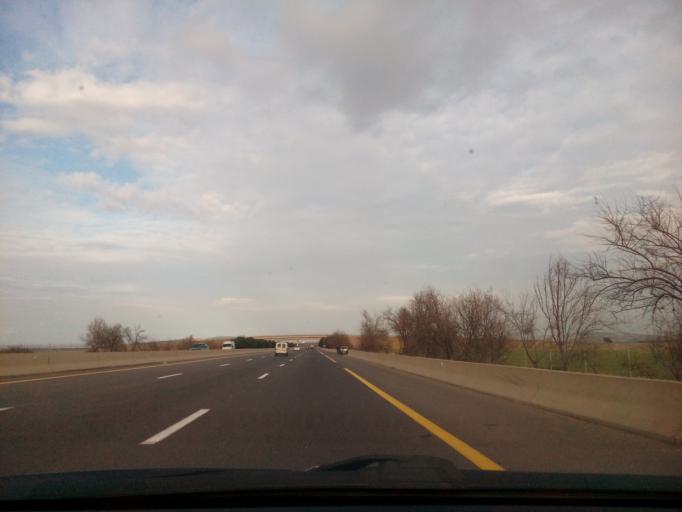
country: DZ
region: Mostaganem
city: Mostaganem
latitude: 35.6781
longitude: 0.1517
